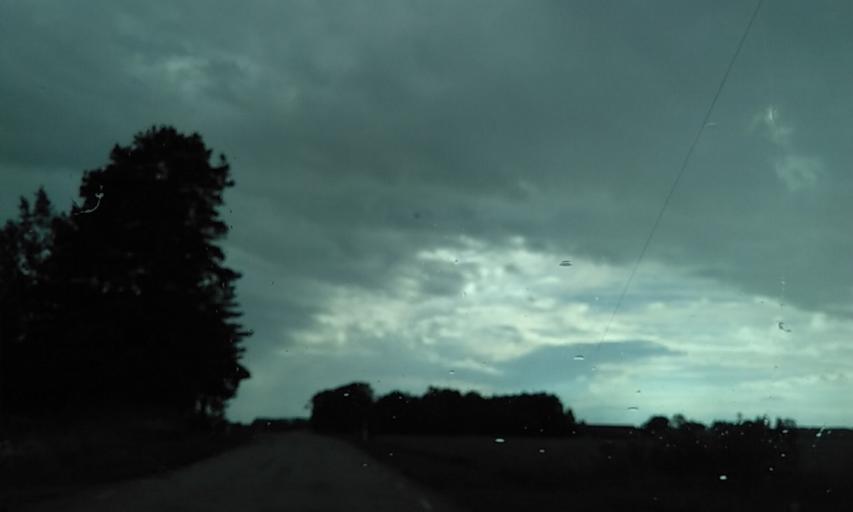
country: SE
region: Vaestra Goetaland
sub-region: Grastorps Kommun
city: Graestorp
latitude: 58.4413
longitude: 12.7643
